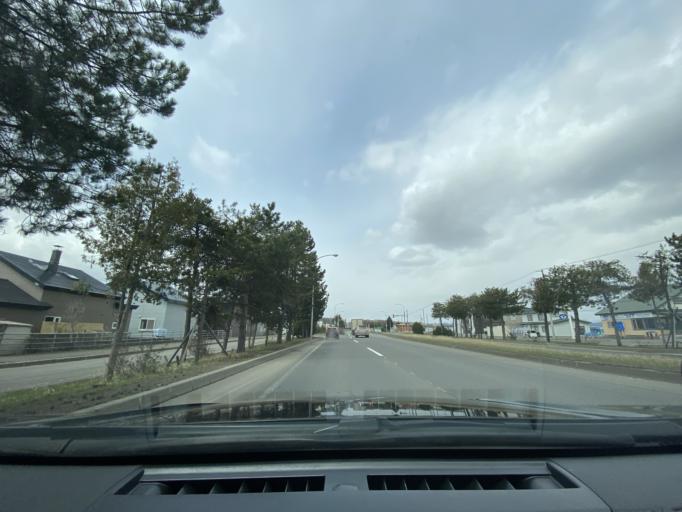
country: JP
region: Hokkaido
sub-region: Asahikawa-shi
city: Asahikawa
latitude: 43.8177
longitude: 142.3983
